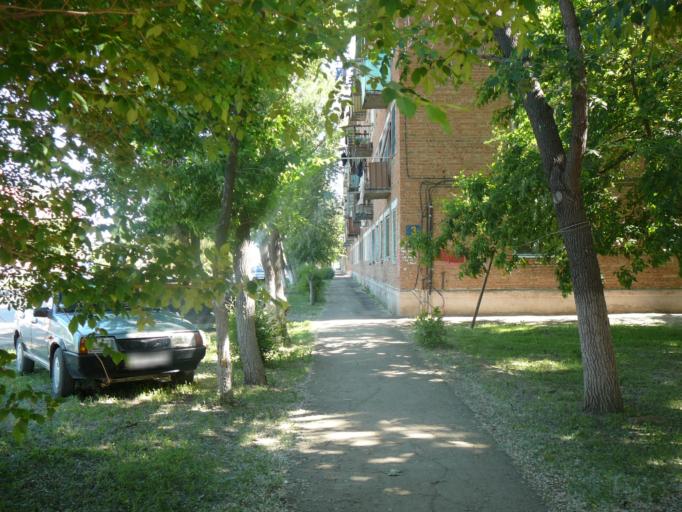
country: RU
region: Saratov
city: Engel's
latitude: 51.4717
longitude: 46.1490
